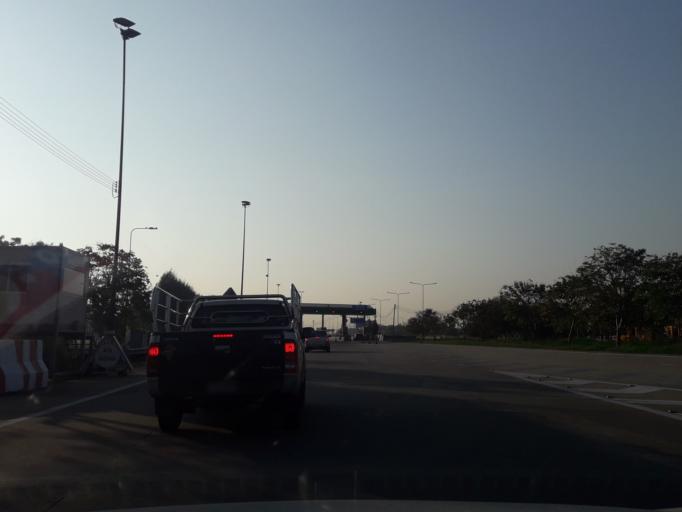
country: TH
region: Phra Nakhon Si Ayutthaya
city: Bang Pa-in
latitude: 14.1459
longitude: 100.5566
